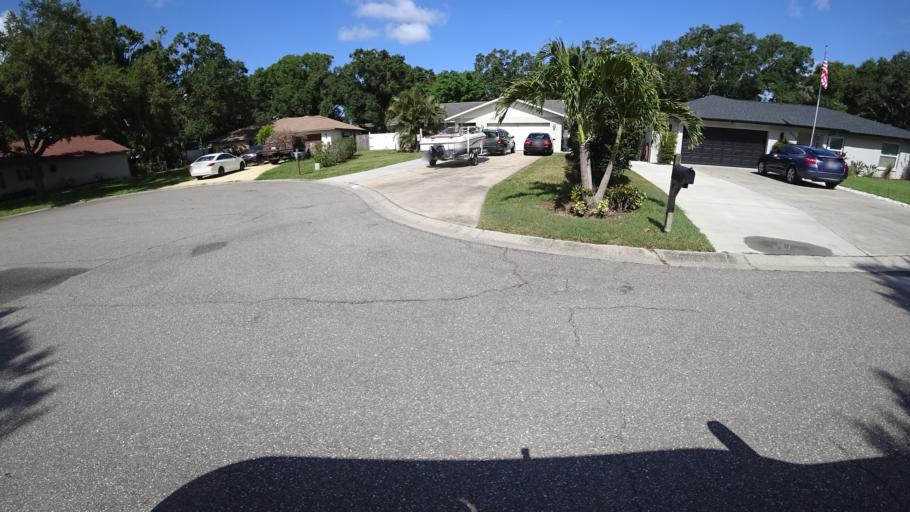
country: US
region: Florida
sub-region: Sarasota County
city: Desoto Lakes
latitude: 27.3914
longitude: -82.4994
